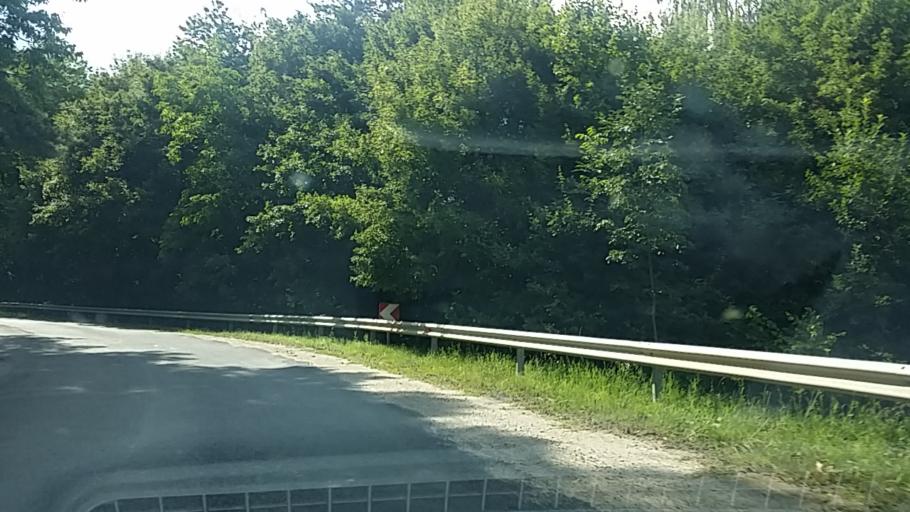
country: HU
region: Zala
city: Becsehely
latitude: 46.5205
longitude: 16.7394
